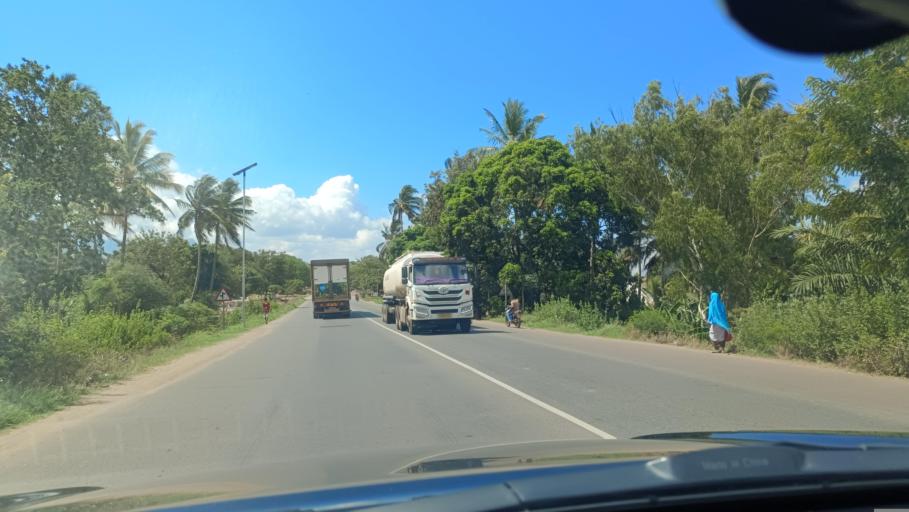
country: TZ
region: Morogoro
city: Morogoro
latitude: -6.8139
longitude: 37.6499
